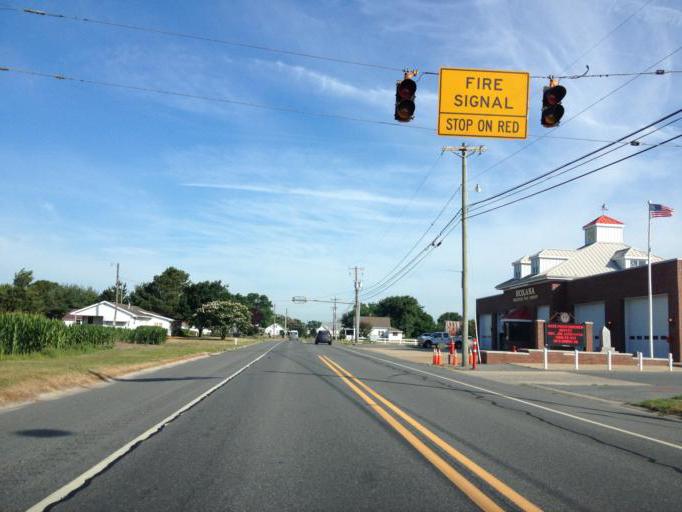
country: US
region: Delaware
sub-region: Sussex County
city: Selbyville
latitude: 38.4907
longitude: -75.1638
